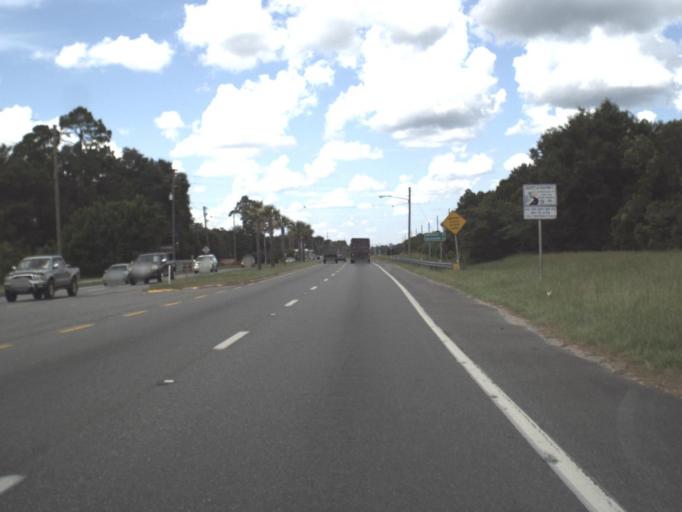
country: US
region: Florida
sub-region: Taylor County
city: Perry
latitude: 30.1194
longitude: -83.5904
